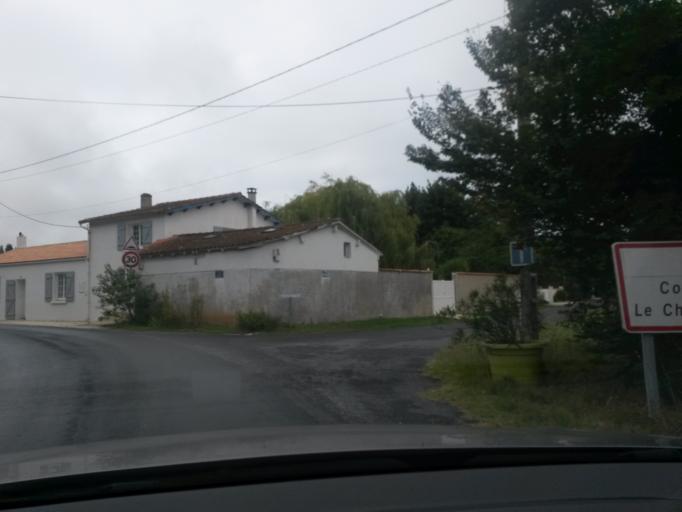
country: FR
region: Poitou-Charentes
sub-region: Departement de la Charente-Maritime
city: Saint-Trojan-les-Bains
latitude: 45.8749
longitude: -1.2060
